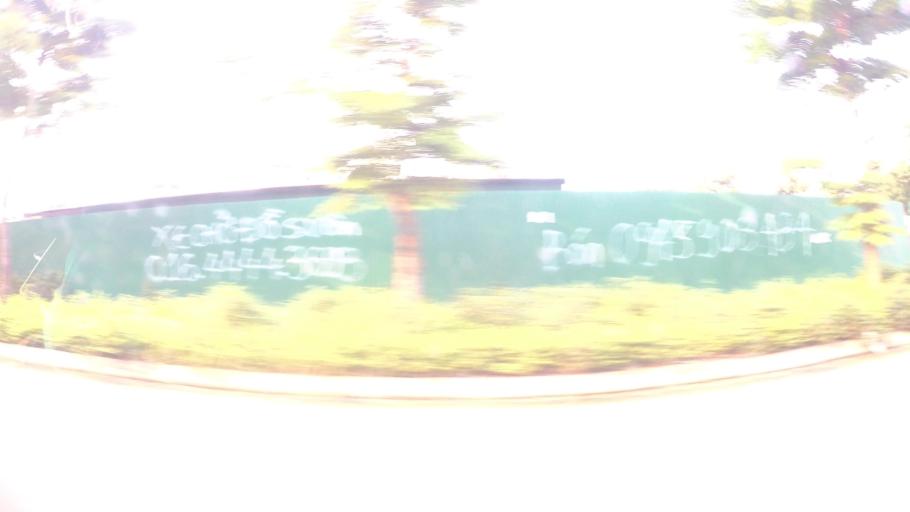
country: VN
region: Ha Noi
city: Thanh Xuan
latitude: 20.9768
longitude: 105.8165
